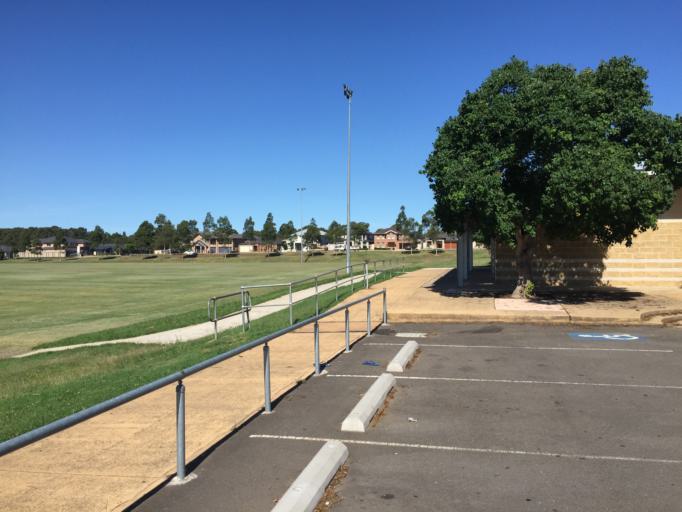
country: AU
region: New South Wales
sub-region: Blacktown
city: Stanhope Gardens
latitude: -33.7211
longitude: 150.9062
